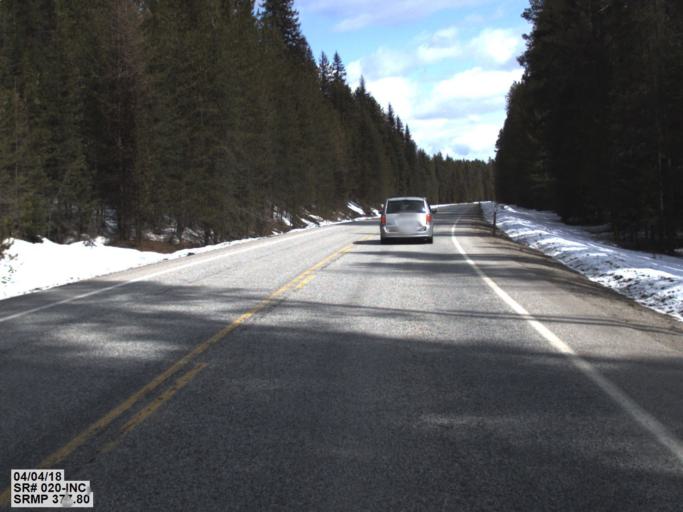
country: US
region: Washington
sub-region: Stevens County
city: Colville
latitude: 48.5944
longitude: -117.5595
